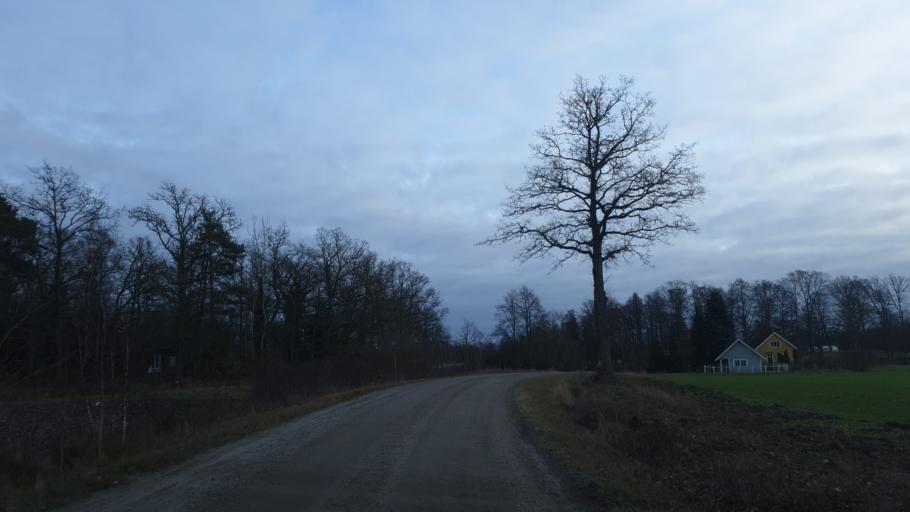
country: SE
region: Kalmar
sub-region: Torsas Kommun
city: Torsas
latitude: 56.3109
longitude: 16.0393
